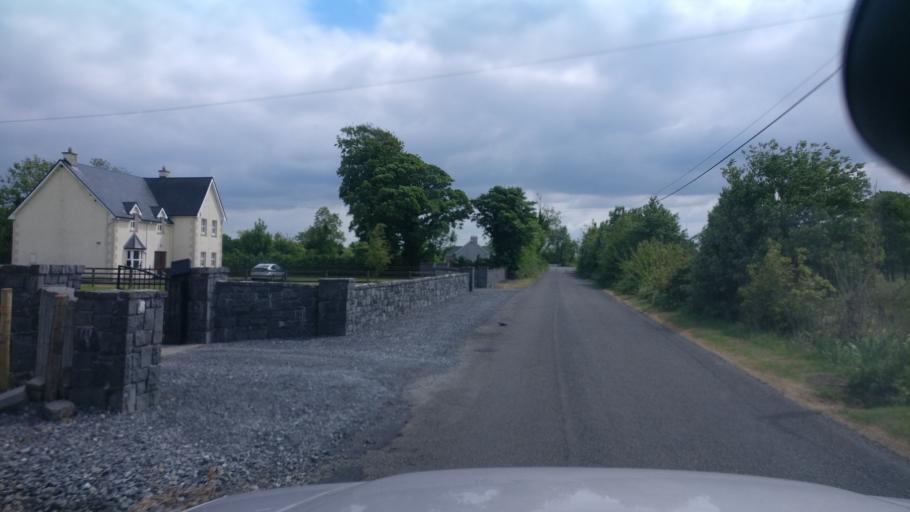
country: IE
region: Connaught
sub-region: County Galway
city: Ballinasloe
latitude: 53.2797
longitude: -8.3390
